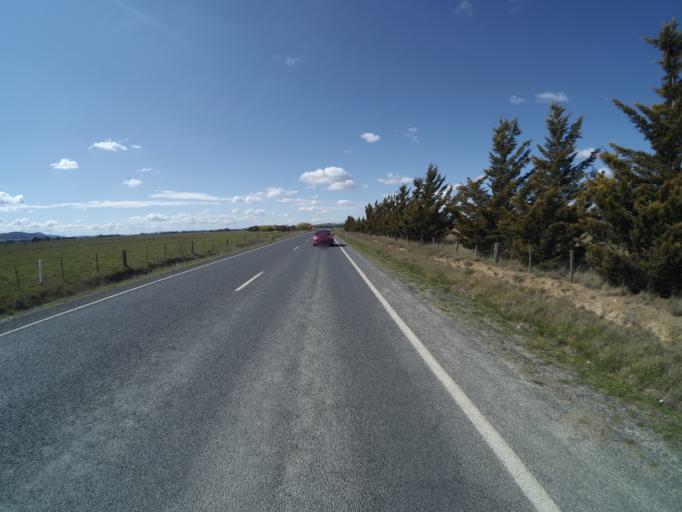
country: AU
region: New South Wales
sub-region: Palerang
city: Bungendore
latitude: -35.2749
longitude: 149.4259
